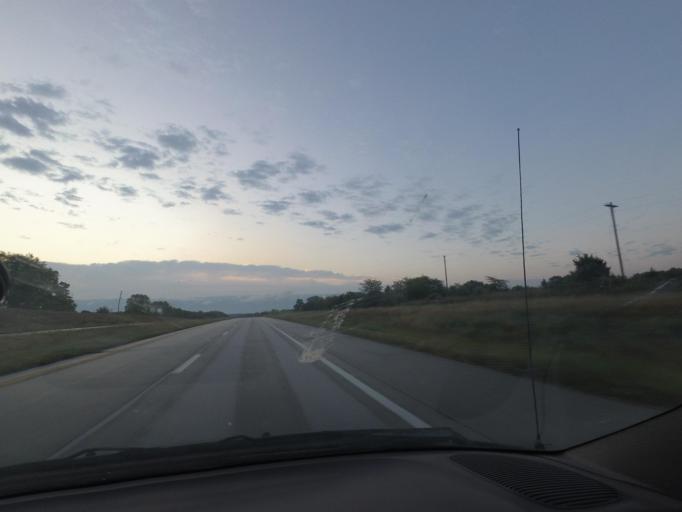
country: US
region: Missouri
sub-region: Macon County
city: Macon
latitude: 39.7533
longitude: -92.5352
